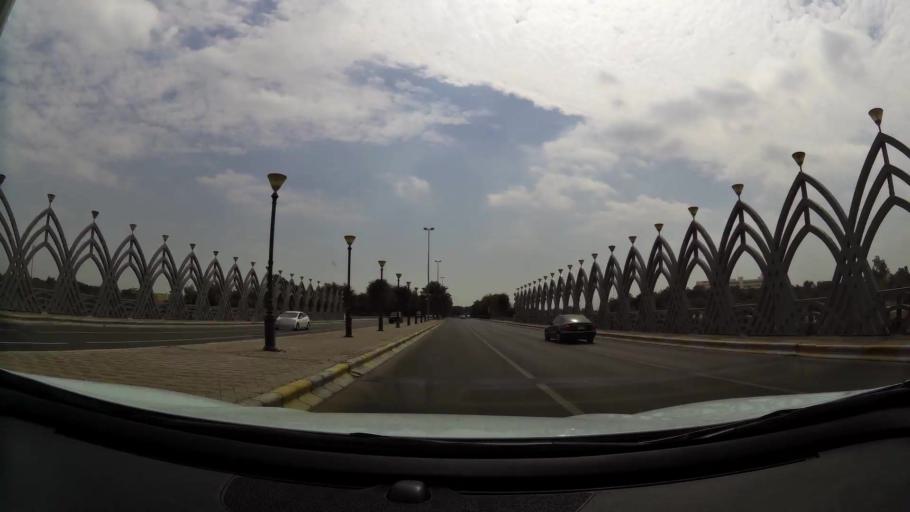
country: AE
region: Abu Dhabi
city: Al Ain
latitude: 24.2106
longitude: 55.7872
